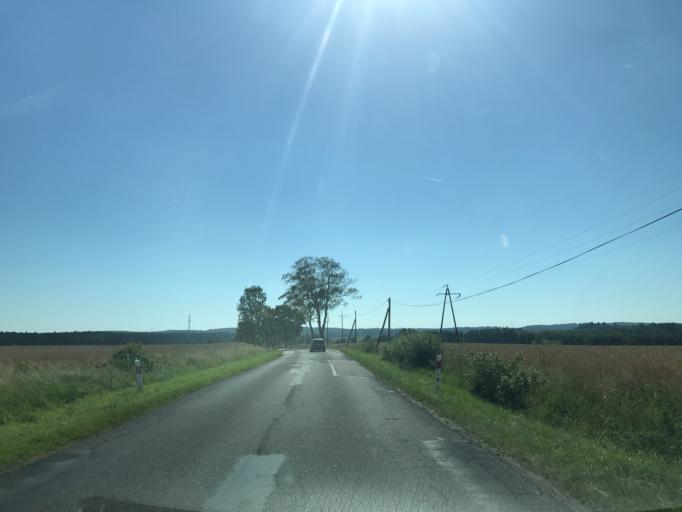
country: PL
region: Pomeranian Voivodeship
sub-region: Powiat bytowski
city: Czarna Dabrowka
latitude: 54.3627
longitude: 17.5216
